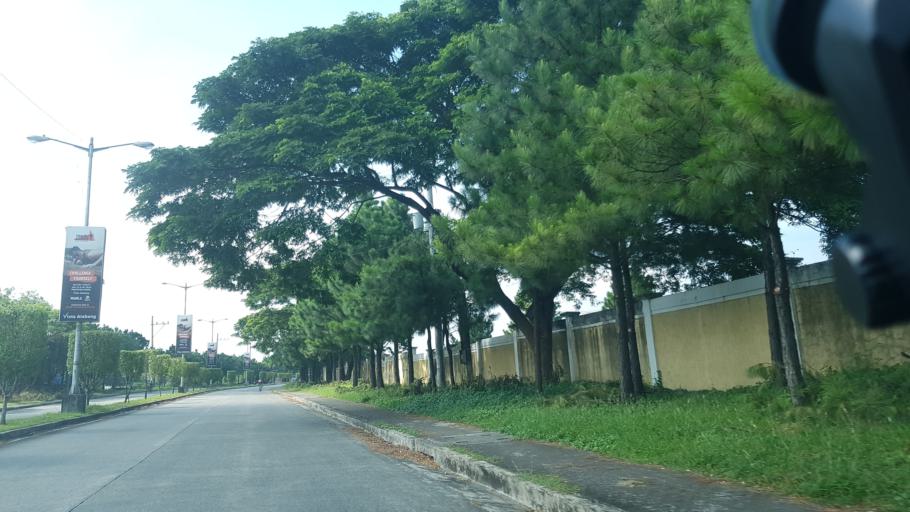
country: PH
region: Calabarzon
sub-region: Province of Laguna
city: Magsaysay
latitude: 14.3574
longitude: 121.0093
